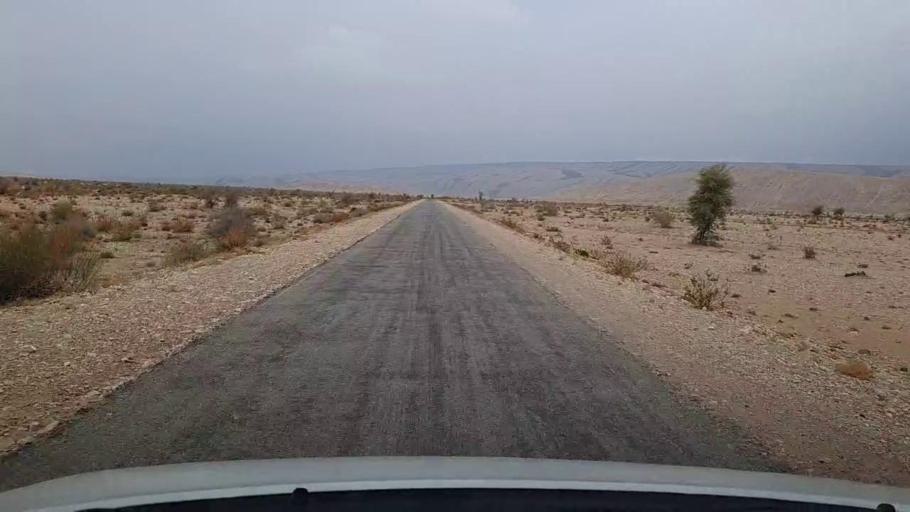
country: PK
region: Sindh
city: Sehwan
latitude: 26.2531
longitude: 67.7197
